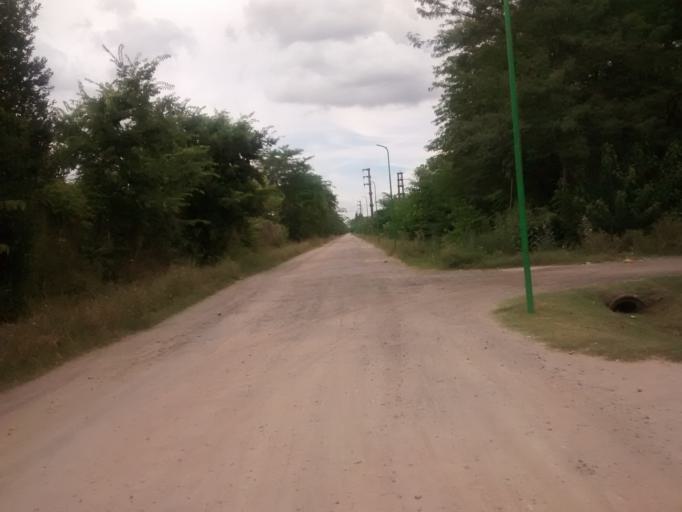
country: AR
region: Buenos Aires
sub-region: Partido de La Plata
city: La Plata
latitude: -34.8610
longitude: -58.0744
